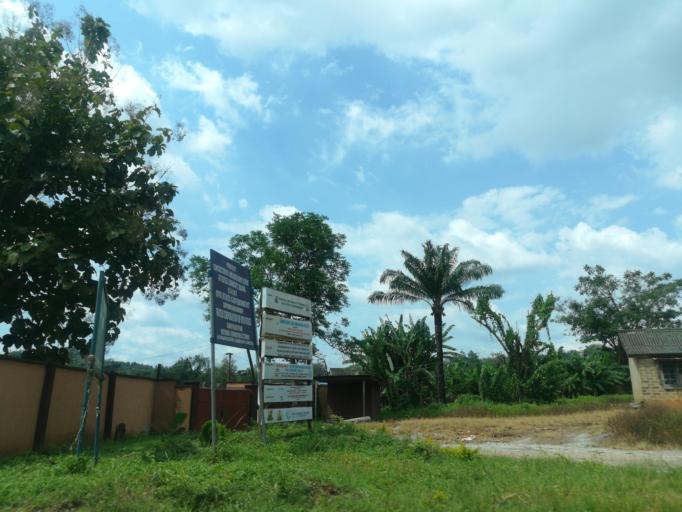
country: NG
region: Oyo
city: Ibadan
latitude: 7.4189
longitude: 3.8564
